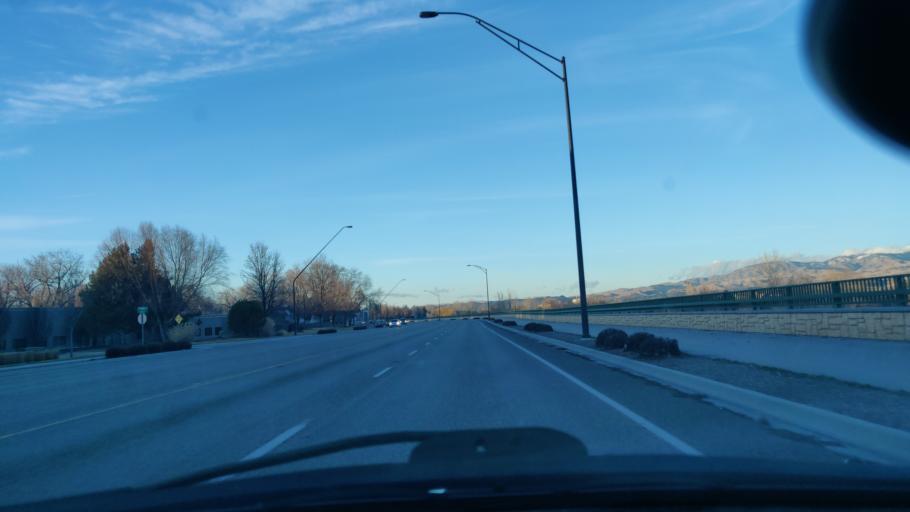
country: US
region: Idaho
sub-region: Ada County
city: Boise
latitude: 43.5798
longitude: -116.1982
